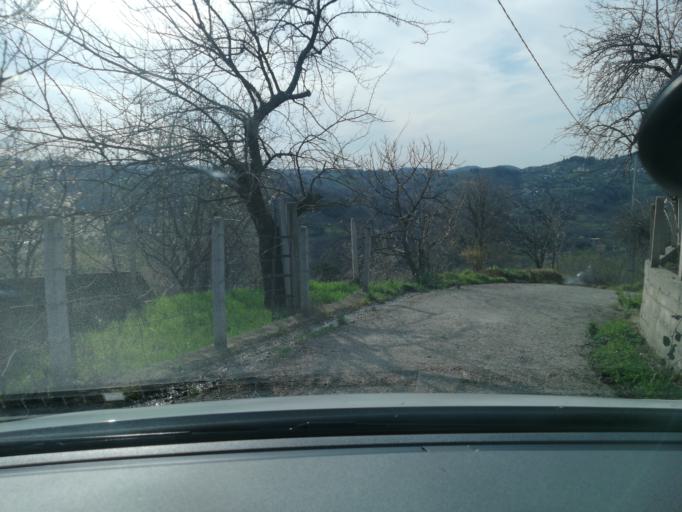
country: TR
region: Zonguldak
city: Kozlu
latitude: 41.3582
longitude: 31.6249
